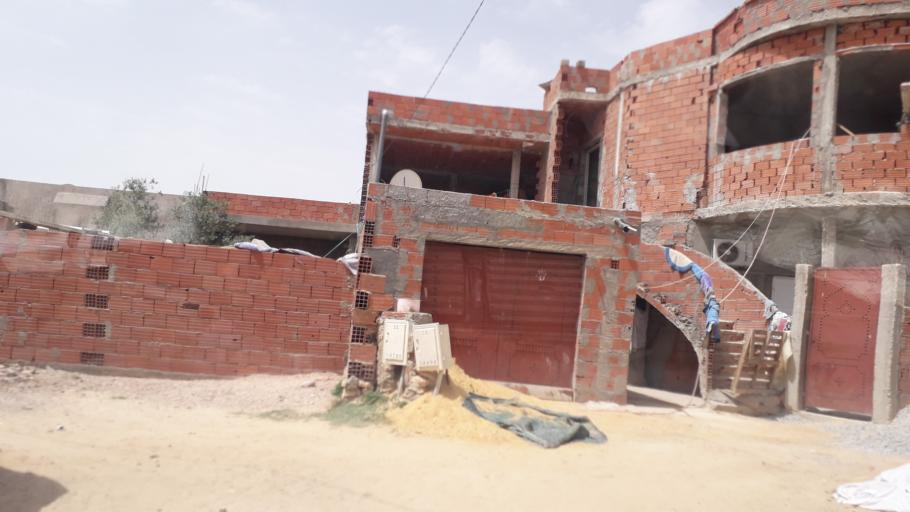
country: TN
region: Safaqis
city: Al Qarmadah
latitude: 34.8436
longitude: 10.7760
